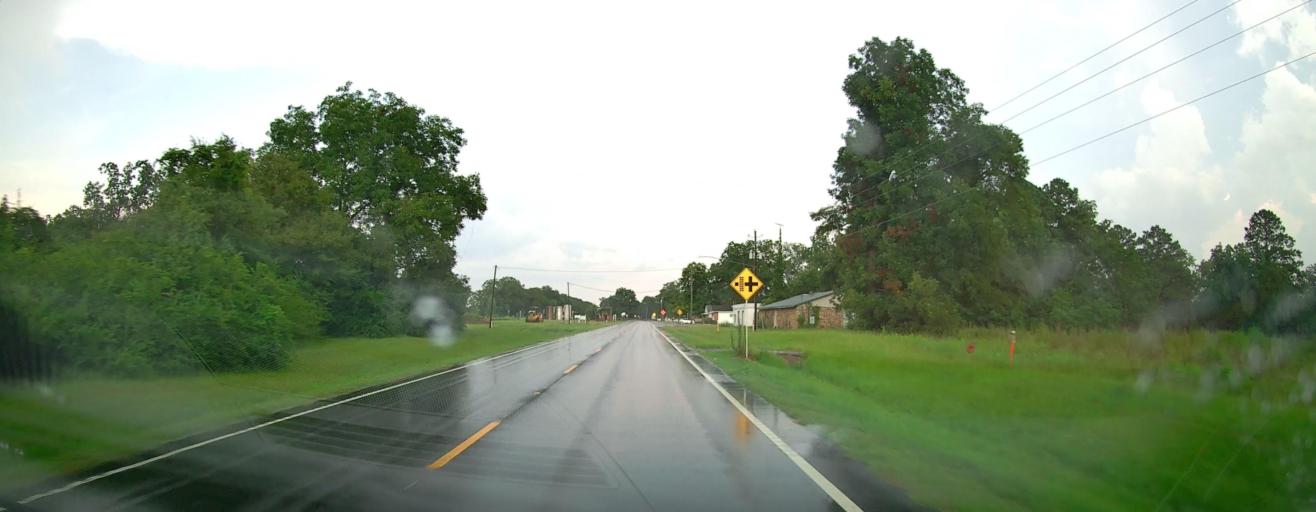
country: US
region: Georgia
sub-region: Dodge County
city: Chester
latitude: 32.5606
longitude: -83.1566
